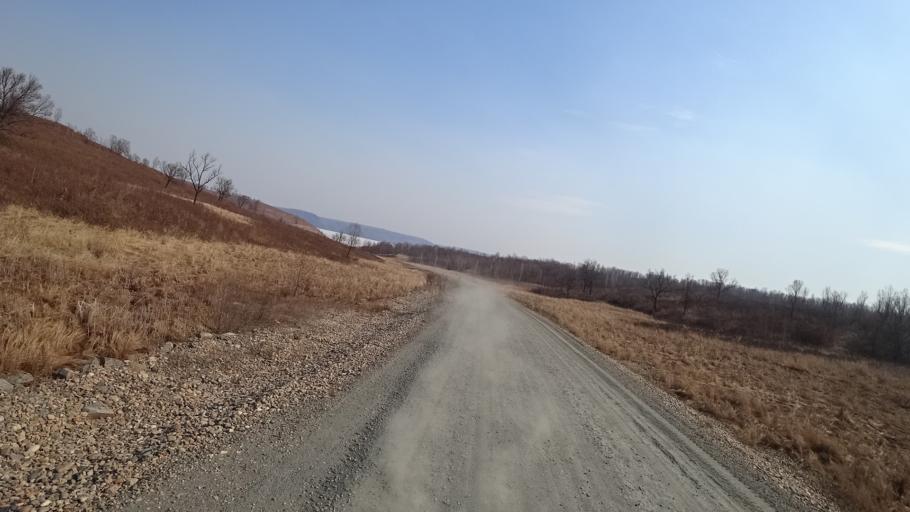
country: RU
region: Amur
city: Novobureyskiy
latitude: 49.8238
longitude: 129.9966
